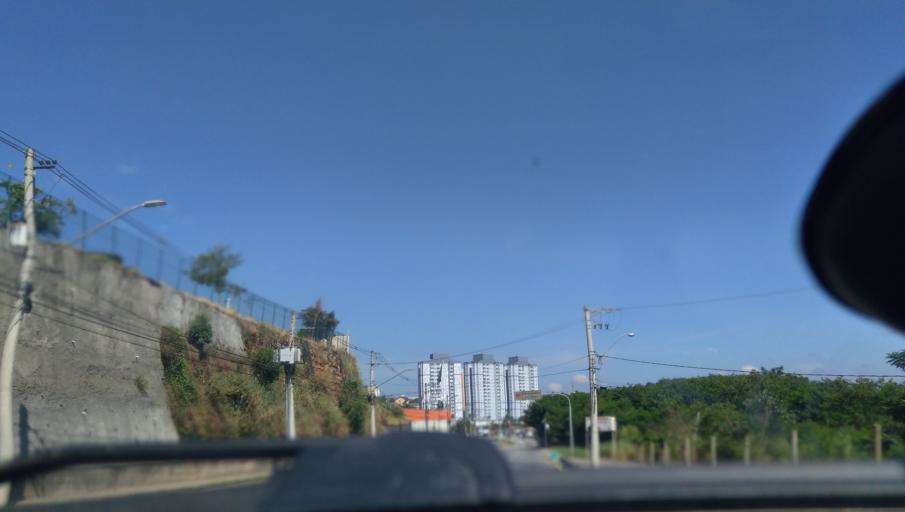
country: BR
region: Sao Paulo
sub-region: Sao Jose Dos Campos
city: Sao Jose dos Campos
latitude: -23.1793
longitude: -45.8648
